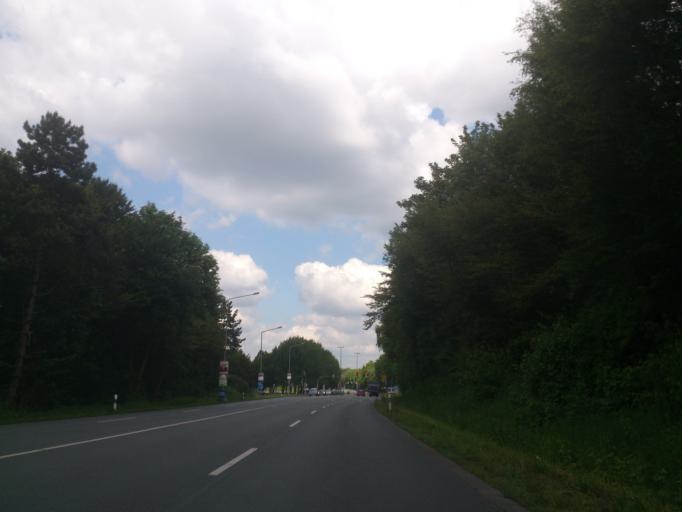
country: DE
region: North Rhine-Westphalia
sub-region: Regierungsbezirk Detmold
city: Paderborn
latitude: 51.7139
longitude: 8.7203
